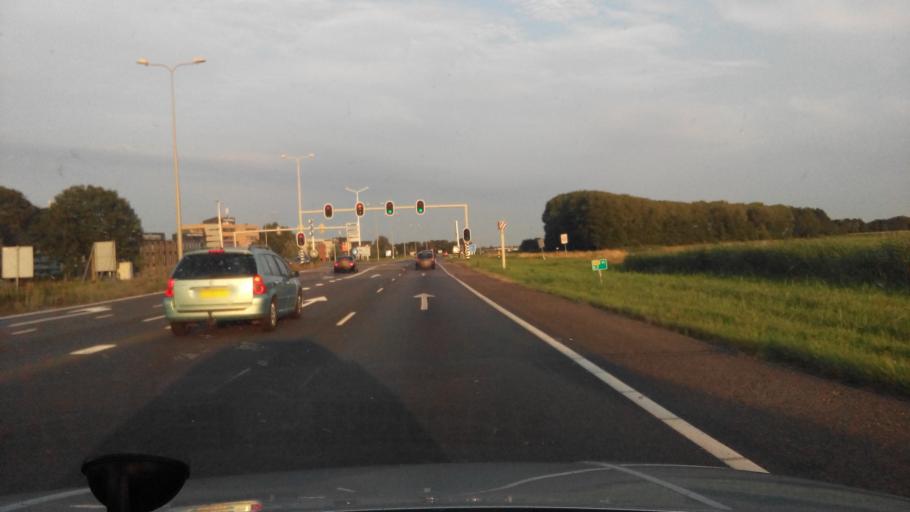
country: NL
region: South Holland
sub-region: Gemeente Alphen aan den Rijn
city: Alphen aan den Rijn
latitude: 52.1239
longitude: 4.6242
